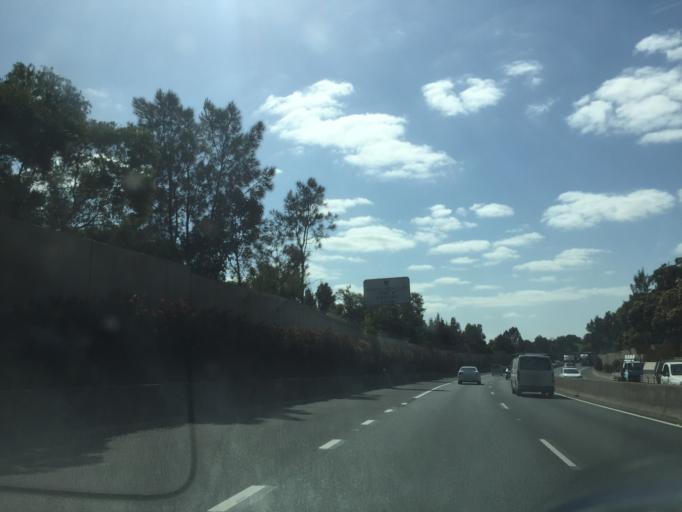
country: AU
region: New South Wales
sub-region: Canterbury
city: Clemton Park
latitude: -33.9403
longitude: 151.0848
